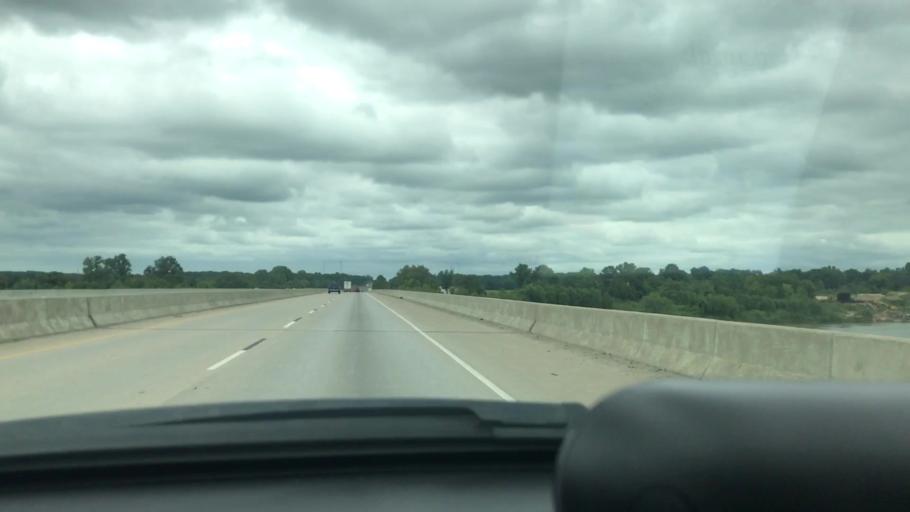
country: US
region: Oklahoma
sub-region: Muskogee County
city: Muskogee
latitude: 35.8071
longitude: -95.4020
